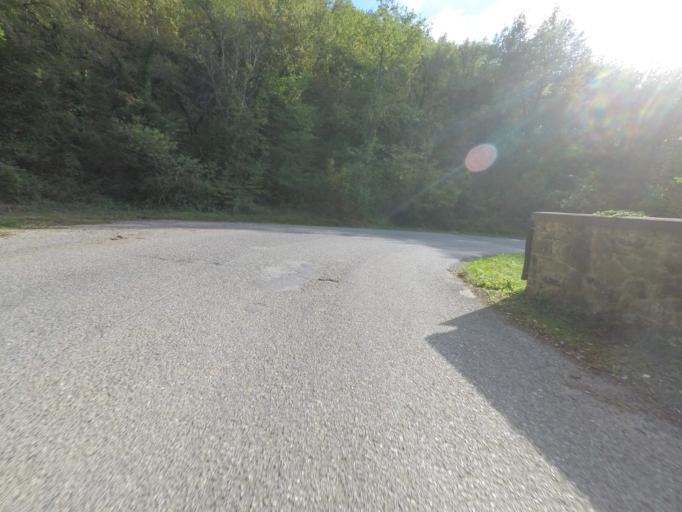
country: IT
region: Tuscany
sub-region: Provincia di Siena
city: Radda in Chianti
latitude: 43.5102
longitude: 11.4055
